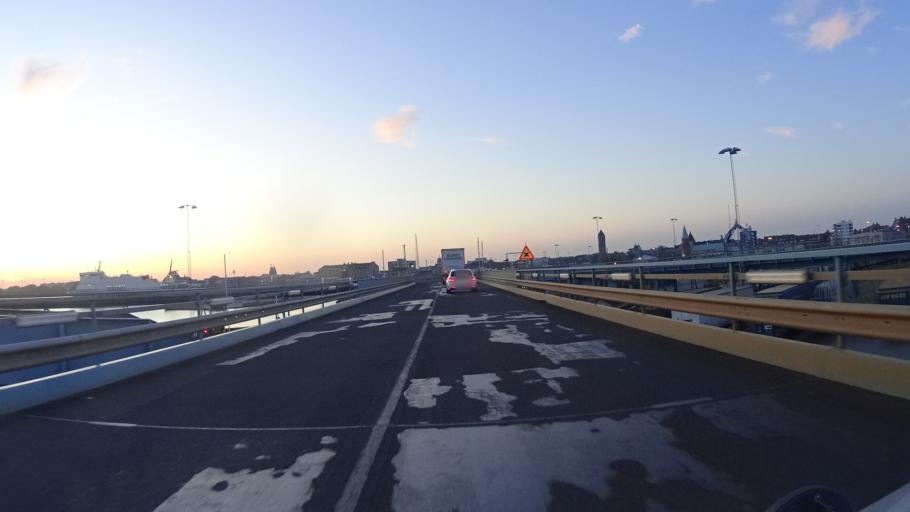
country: SE
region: Skane
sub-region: Trelleborgs Kommun
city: Trelleborg
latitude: 55.3684
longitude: 13.1568
